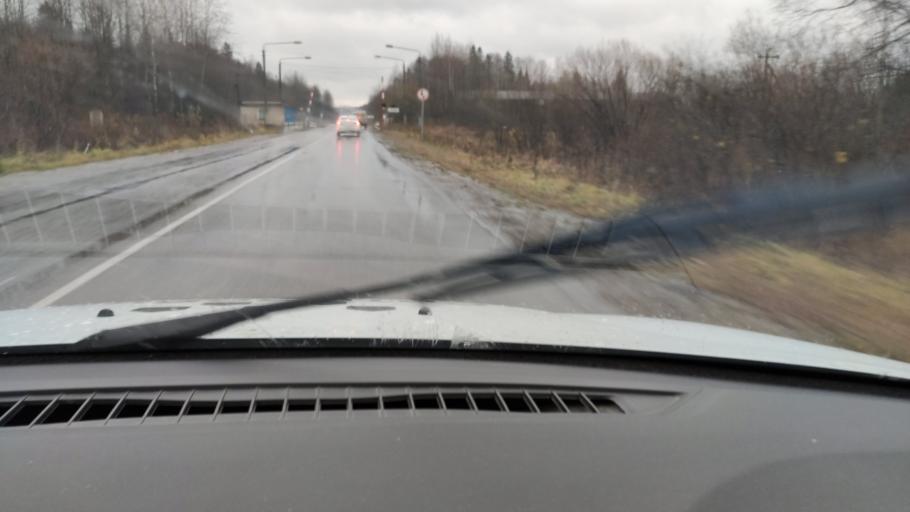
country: RU
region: Perm
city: Novyye Lyady
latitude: 58.0275
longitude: 56.6277
